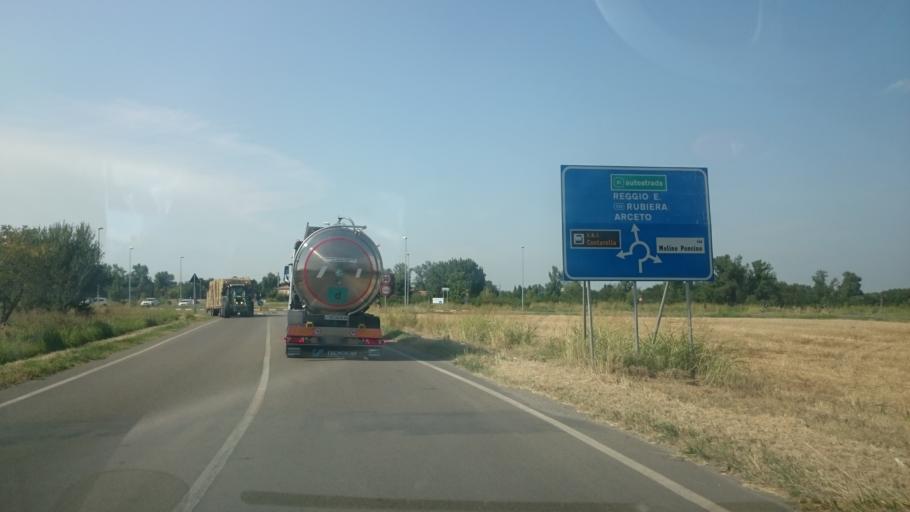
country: IT
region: Emilia-Romagna
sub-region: Provincia di Reggio Emilia
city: Fellegara
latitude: 44.6039
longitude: 10.7049
